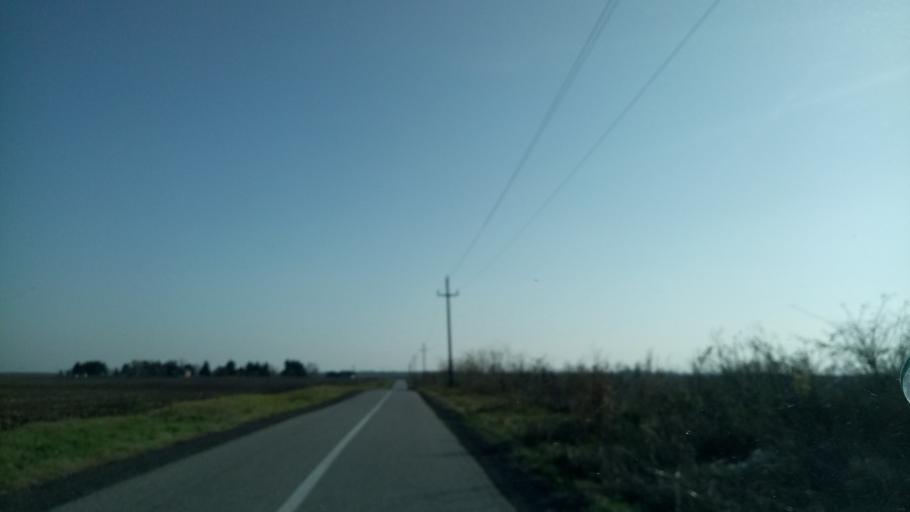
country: RS
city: Ljukovo
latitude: 45.0332
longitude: 20.0448
